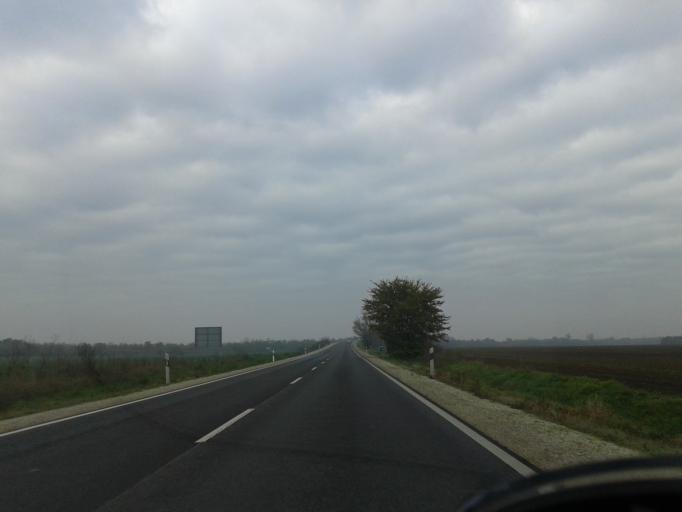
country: HU
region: Fejer
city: Ercsi
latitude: 47.2720
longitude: 18.8815
